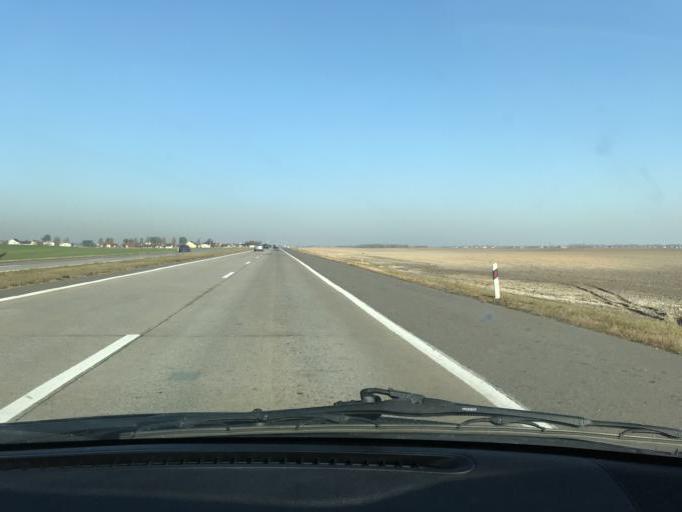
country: BY
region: Minsk
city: Samakhvalavichy
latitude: 53.6685
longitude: 27.4909
